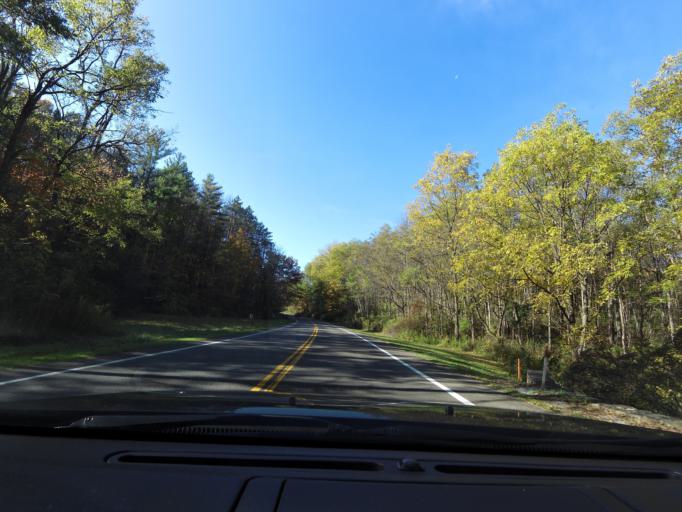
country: US
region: New York
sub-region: Wyoming County
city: Perry
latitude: 42.6970
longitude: -77.9521
